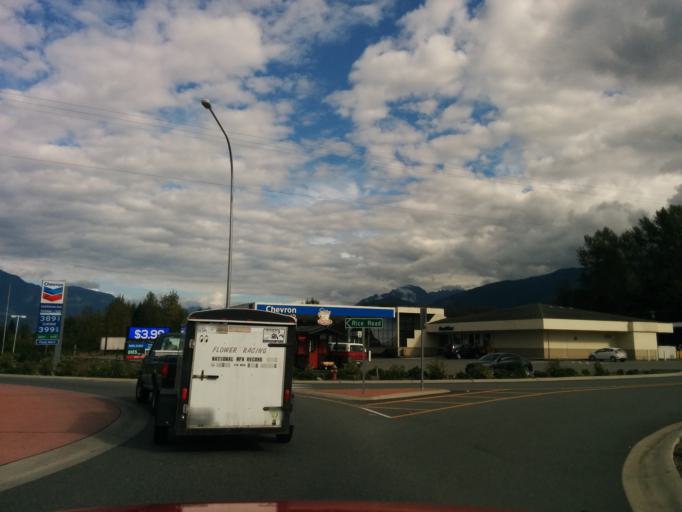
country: US
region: Washington
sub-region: Snohomish County
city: Sultan
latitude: 47.8678
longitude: -121.7778
